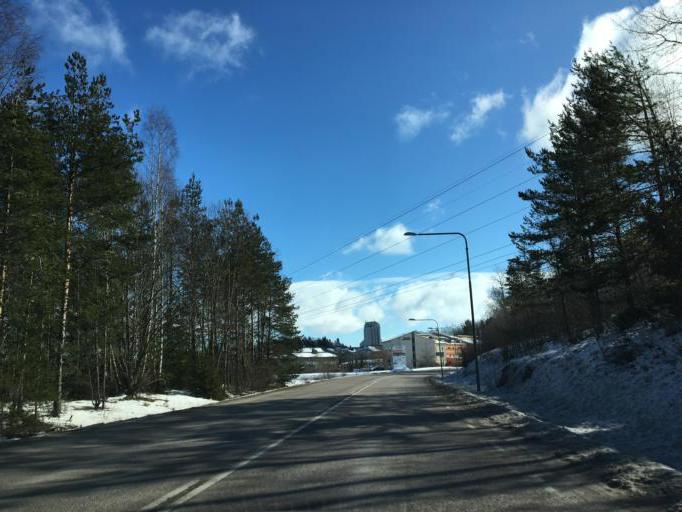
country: SE
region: Vaestmanland
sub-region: Vasteras
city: Vasteras
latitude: 59.6238
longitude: 16.4918
